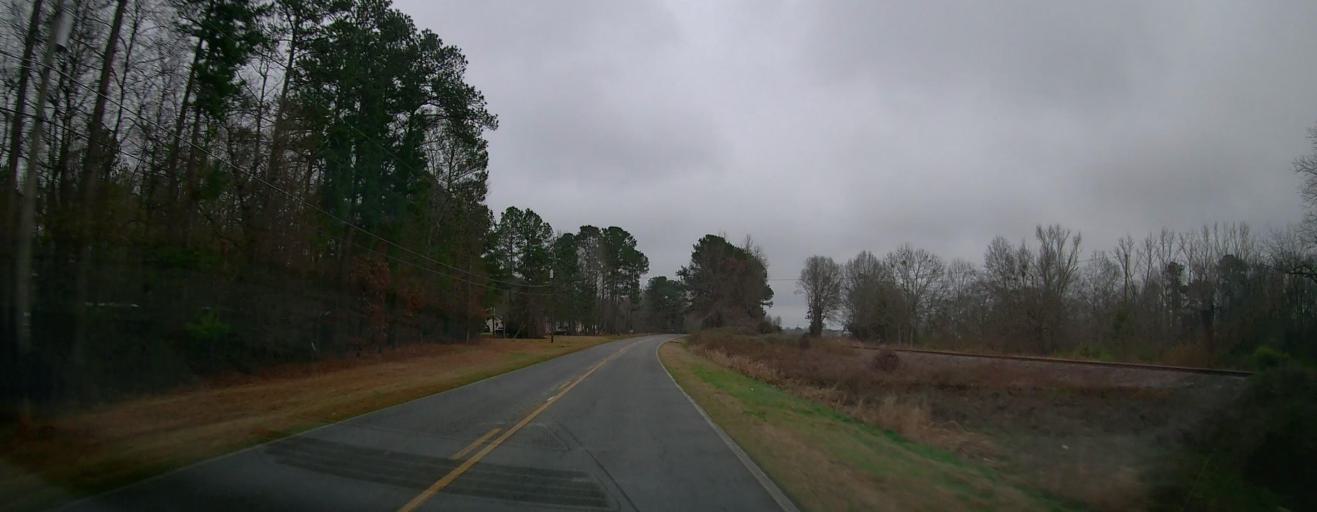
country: US
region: Georgia
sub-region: Lamar County
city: Barnesville
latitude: 33.1465
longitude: -84.1977
